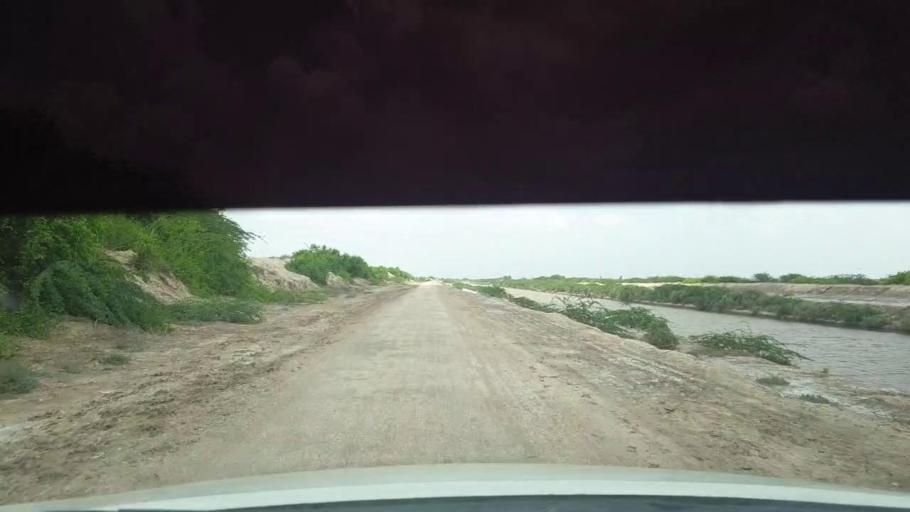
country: PK
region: Sindh
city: Kadhan
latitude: 24.5094
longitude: 69.1189
